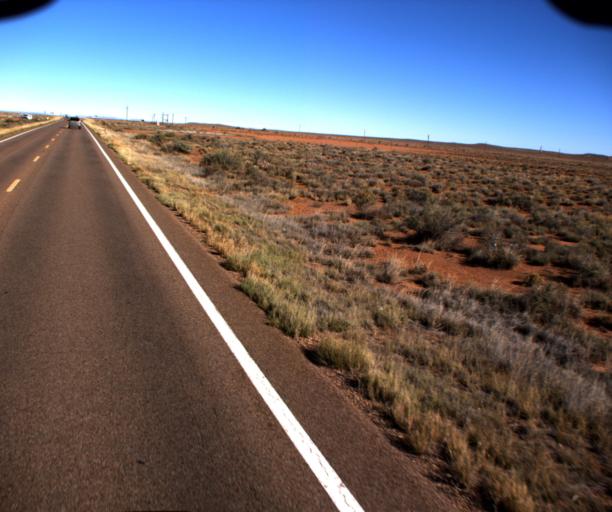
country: US
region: Arizona
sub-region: Navajo County
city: Holbrook
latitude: 34.7931
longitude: -110.1334
